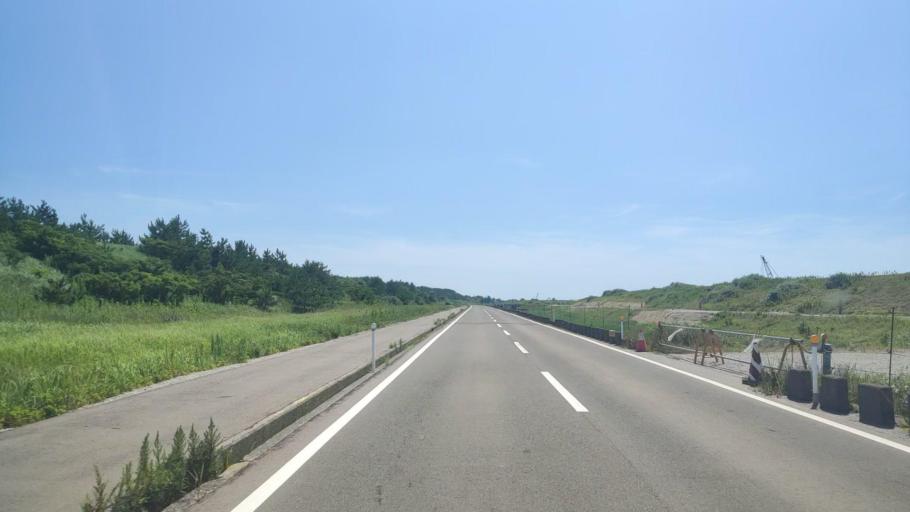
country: JP
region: Ishikawa
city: Kanazawa-shi
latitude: 36.6146
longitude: 136.6001
